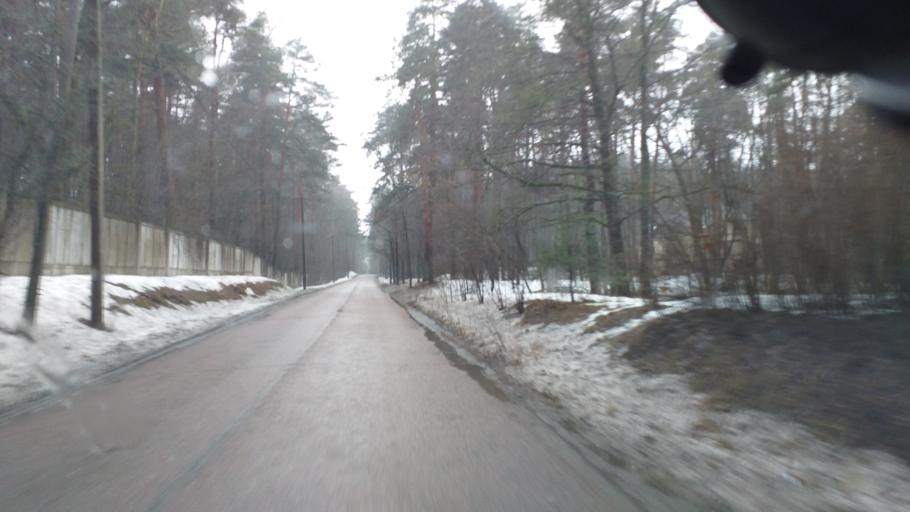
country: LV
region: Riga
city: Bolderaja
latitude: 56.9853
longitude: 24.0235
